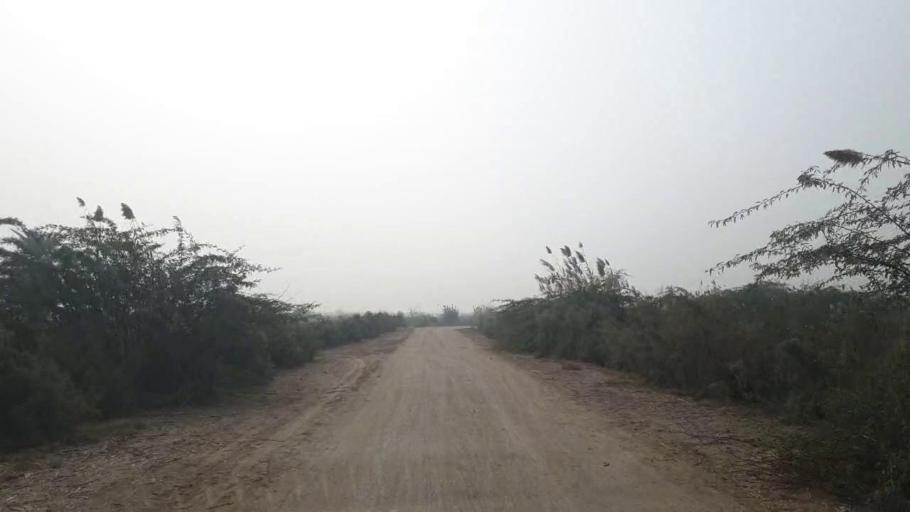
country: PK
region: Sindh
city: Bhit Shah
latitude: 25.7907
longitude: 68.5581
